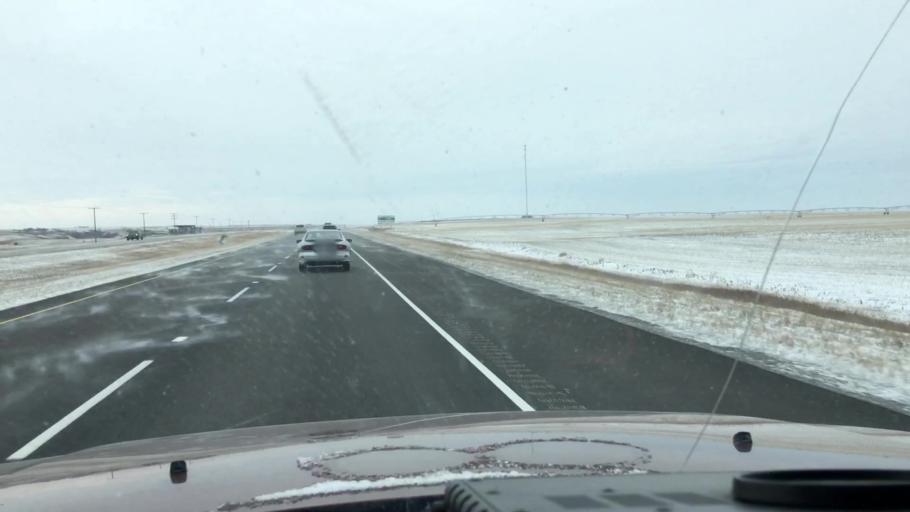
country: CA
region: Saskatchewan
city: Saskatoon
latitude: 51.7471
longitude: -106.4764
